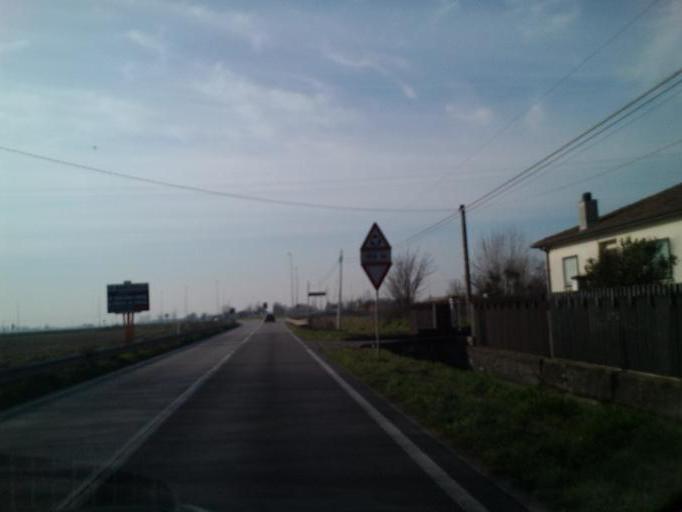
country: IT
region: Lombardy
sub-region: Provincia di Mantova
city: Roverbella
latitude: 45.2523
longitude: 10.8048
